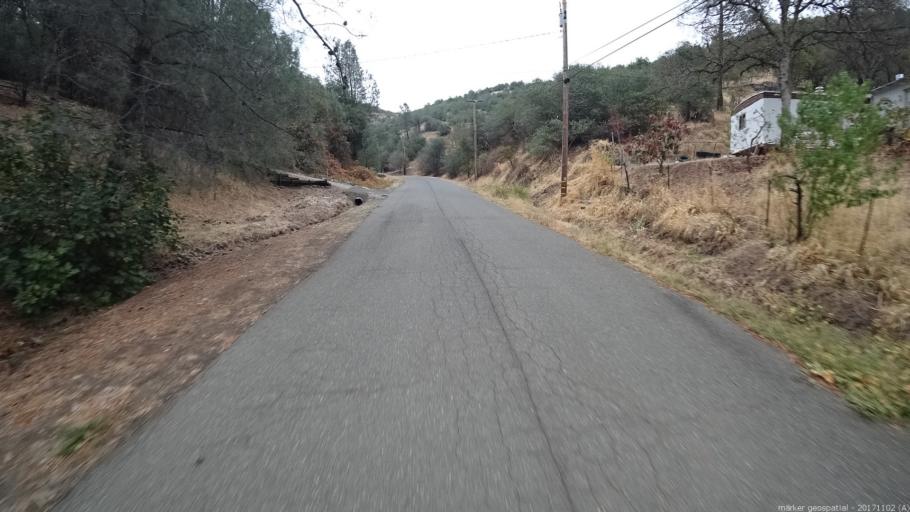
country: US
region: California
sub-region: Shasta County
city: Bella Vista
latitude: 40.7195
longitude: -122.2323
